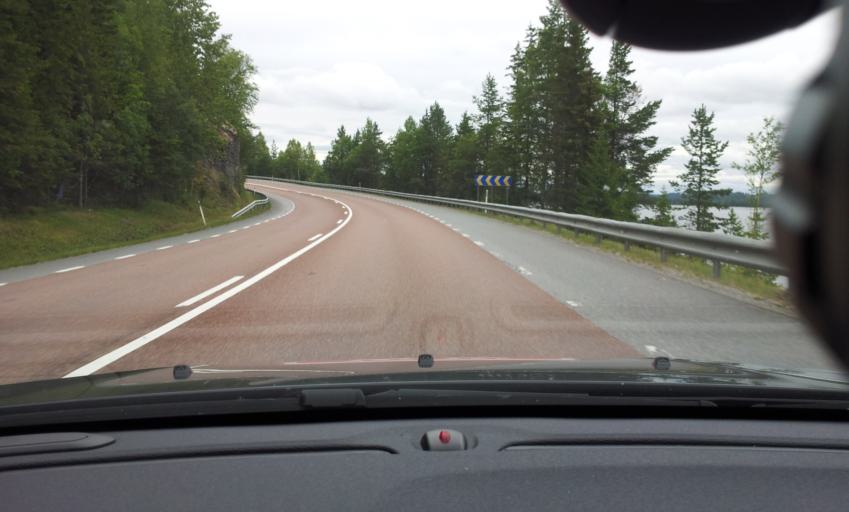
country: SE
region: Jaemtland
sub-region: Braecke Kommun
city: Braecke
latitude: 62.9517
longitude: 15.1606
